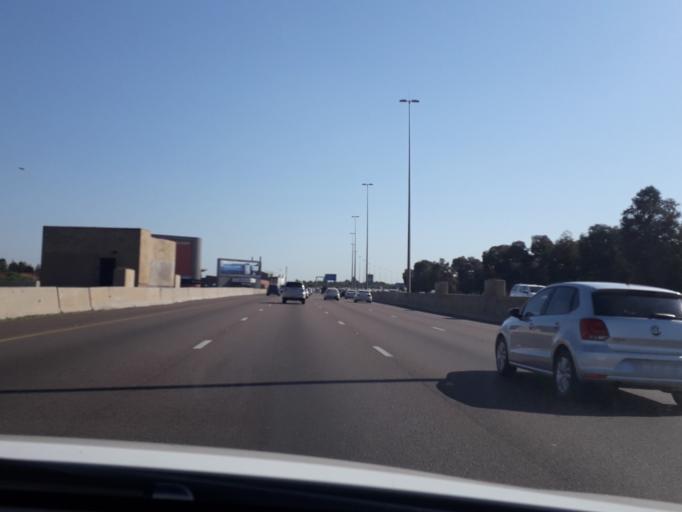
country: ZA
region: Gauteng
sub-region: City of Tshwane Metropolitan Municipality
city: Centurion
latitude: -25.8449
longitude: 28.2301
